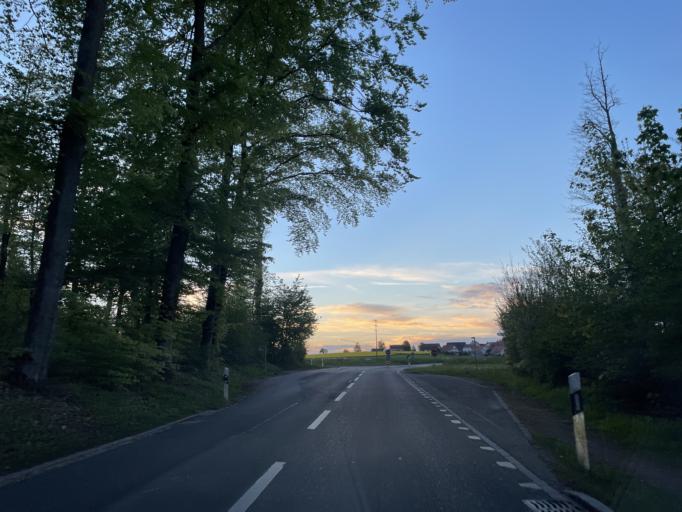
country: CH
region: Zurich
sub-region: Bezirk Winterthur
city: Brutten
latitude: 47.4660
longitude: 8.6769
